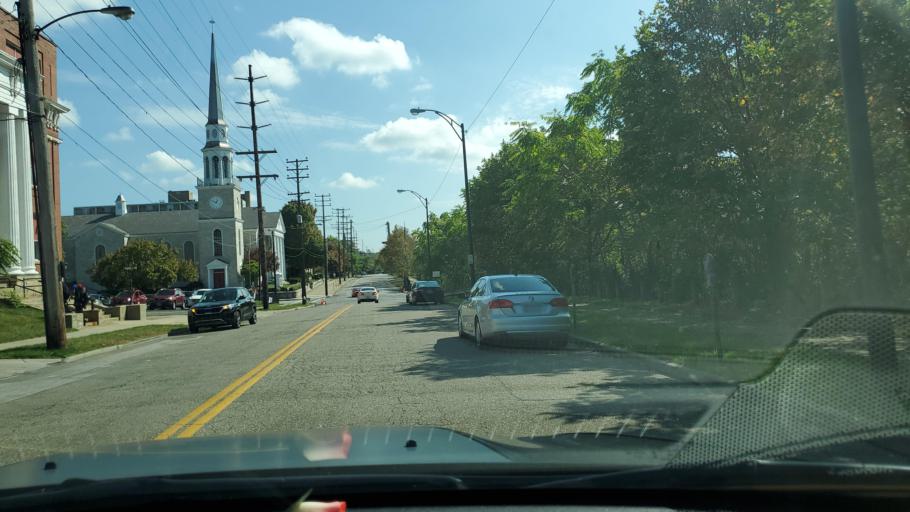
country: US
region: Ohio
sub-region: Mahoning County
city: Youngstown
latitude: 41.1022
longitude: -80.6490
